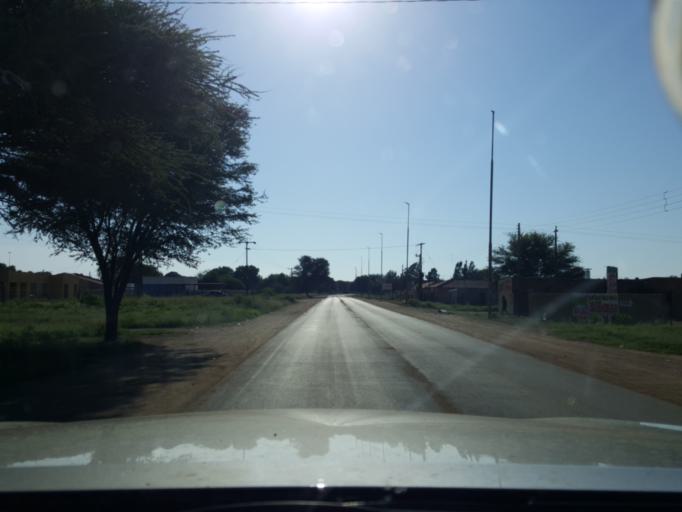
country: ZA
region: North-West
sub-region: Ngaka Modiri Molema District Municipality
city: Mmabatho
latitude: -25.8257
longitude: 25.6381
